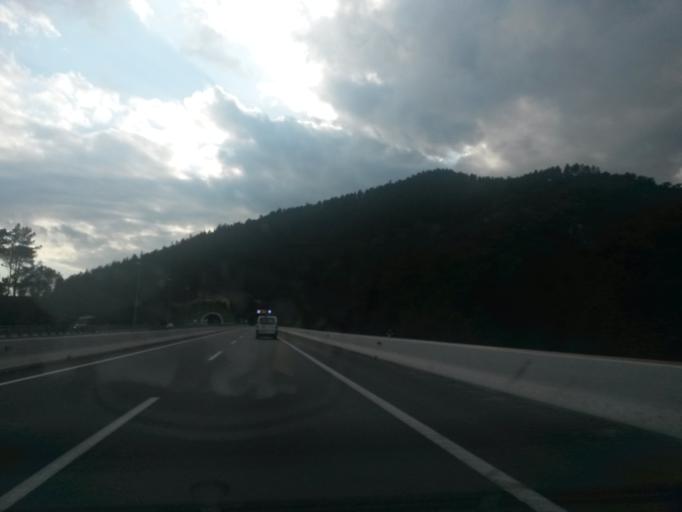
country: ES
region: Catalonia
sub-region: Provincia de Girona
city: Santa Coloma de Farners
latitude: 41.8748
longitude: 2.6098
